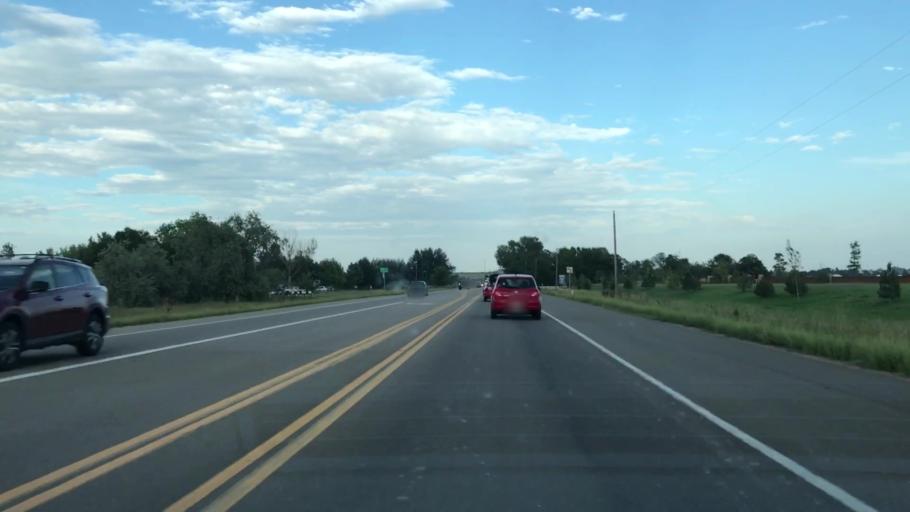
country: US
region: Colorado
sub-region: Boulder County
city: Longmont
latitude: 40.2035
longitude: -105.0640
